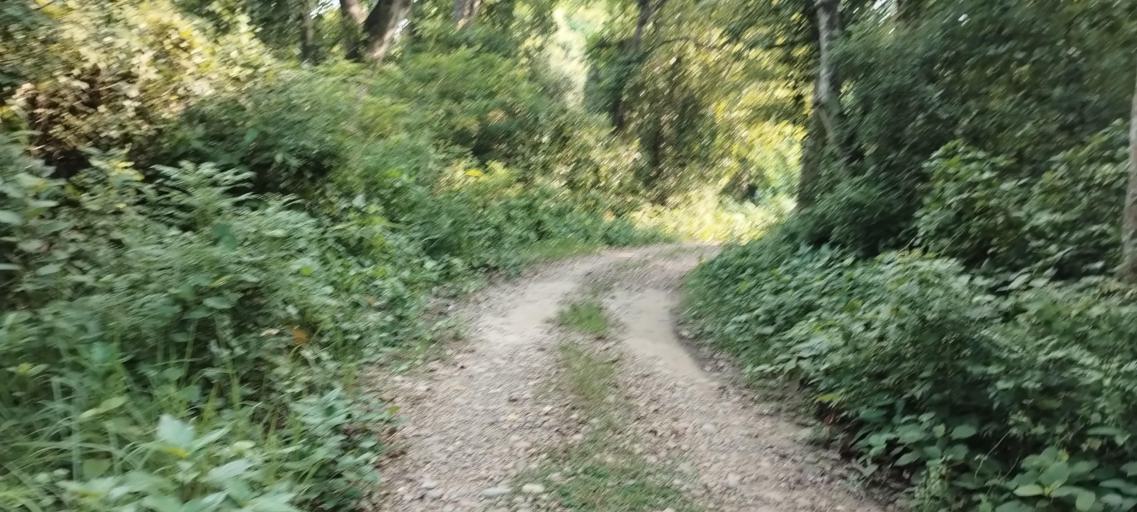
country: NP
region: Far Western
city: Tikapur
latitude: 28.4621
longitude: 81.2406
